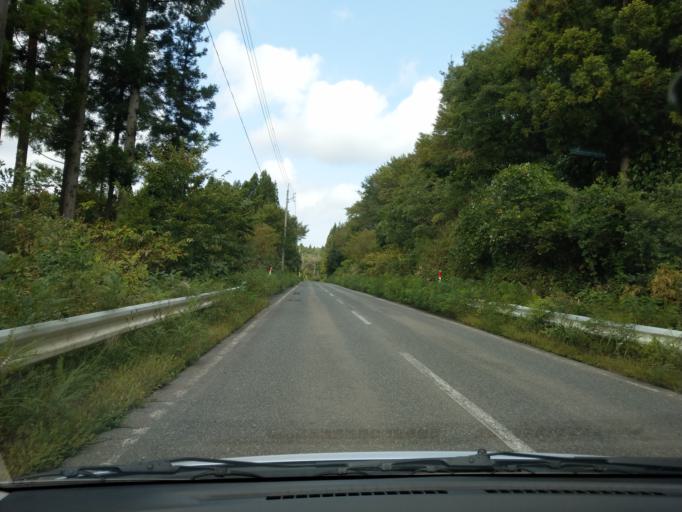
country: JP
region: Akita
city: Omagari
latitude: 39.4598
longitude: 140.3189
